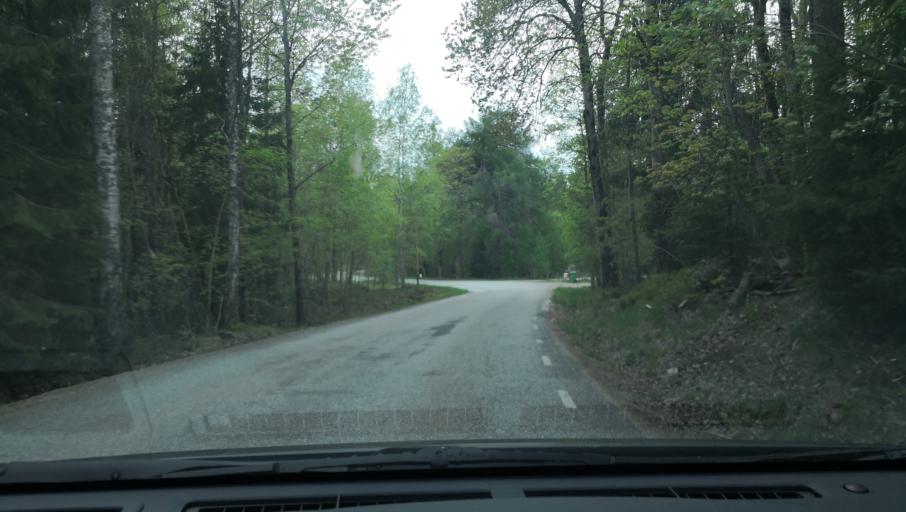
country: SE
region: Vaestmanland
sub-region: Skinnskattebergs Kommun
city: Skinnskatteberg
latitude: 59.8275
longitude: 15.5562
